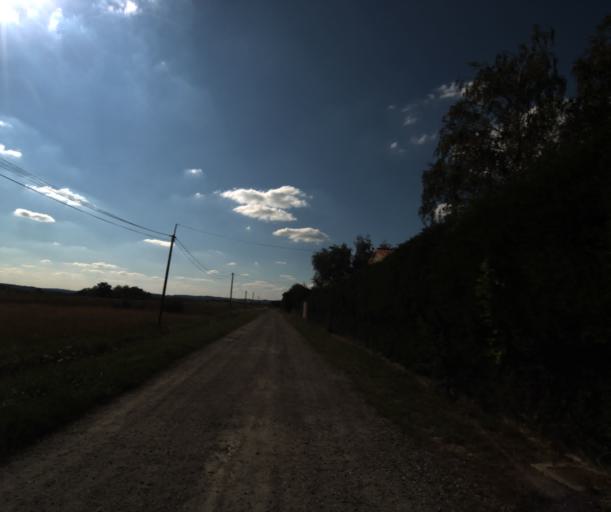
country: FR
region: Midi-Pyrenees
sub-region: Departement de la Haute-Garonne
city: Saint-Lys
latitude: 43.4948
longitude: 1.1904
